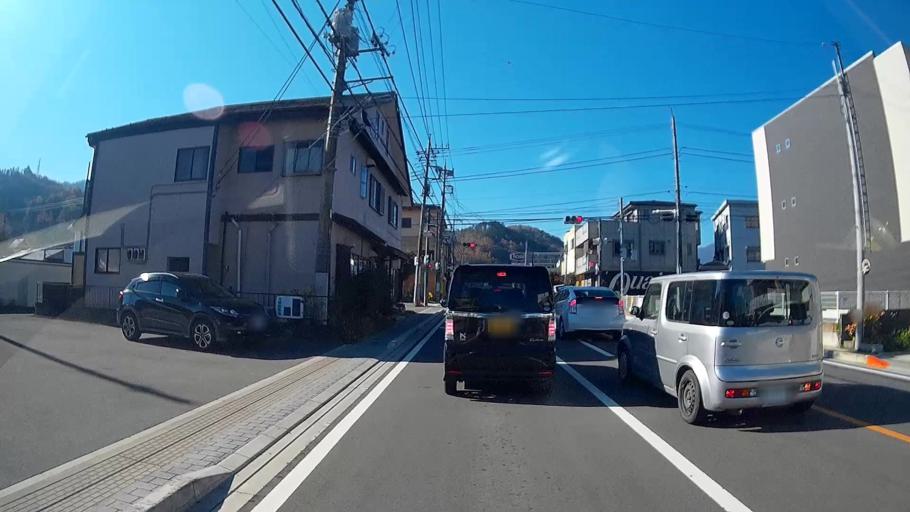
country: JP
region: Yamanashi
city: Otsuki
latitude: 35.5429
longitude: 138.9010
